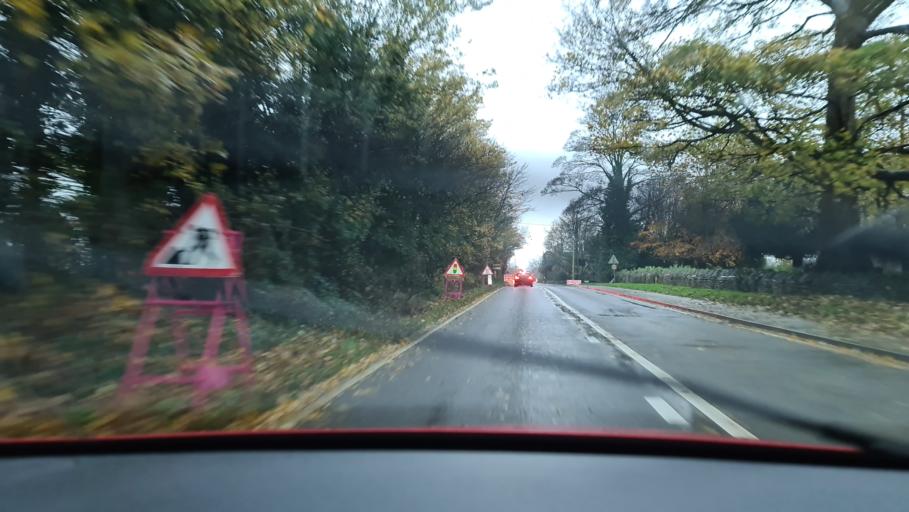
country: GB
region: England
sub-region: Oxfordshire
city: Somerton
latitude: 51.9427
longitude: -1.2116
